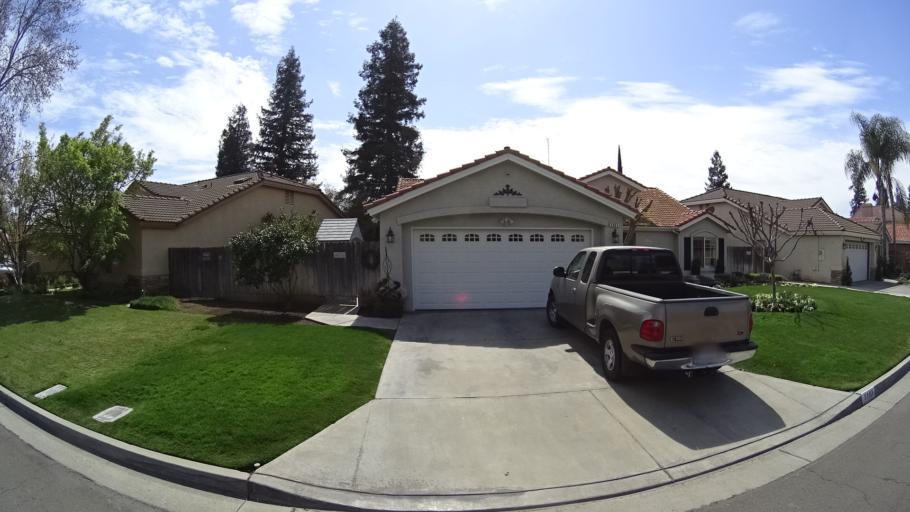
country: US
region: California
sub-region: Fresno County
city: Biola
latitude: 36.8439
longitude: -119.8986
